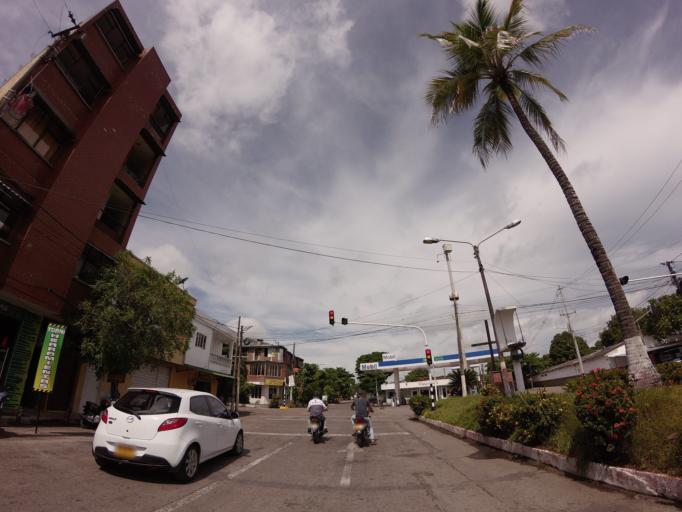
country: CO
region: Caldas
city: La Dorada
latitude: 5.4492
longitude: -74.6671
